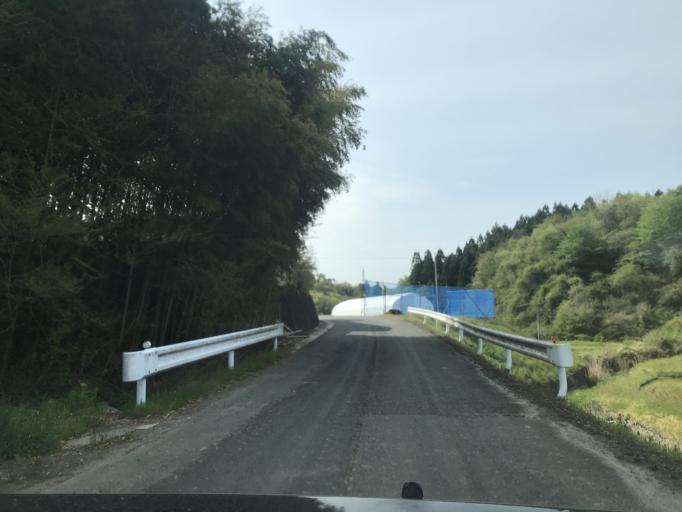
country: JP
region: Iwate
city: Ichinoseki
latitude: 38.8983
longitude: 141.0607
